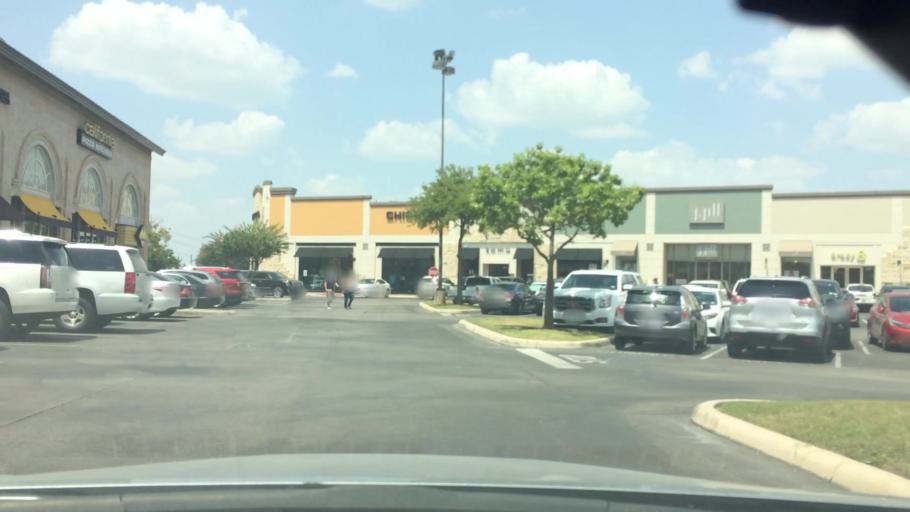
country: US
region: Texas
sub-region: Bexar County
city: Olmos Park
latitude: 29.4972
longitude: -98.4815
